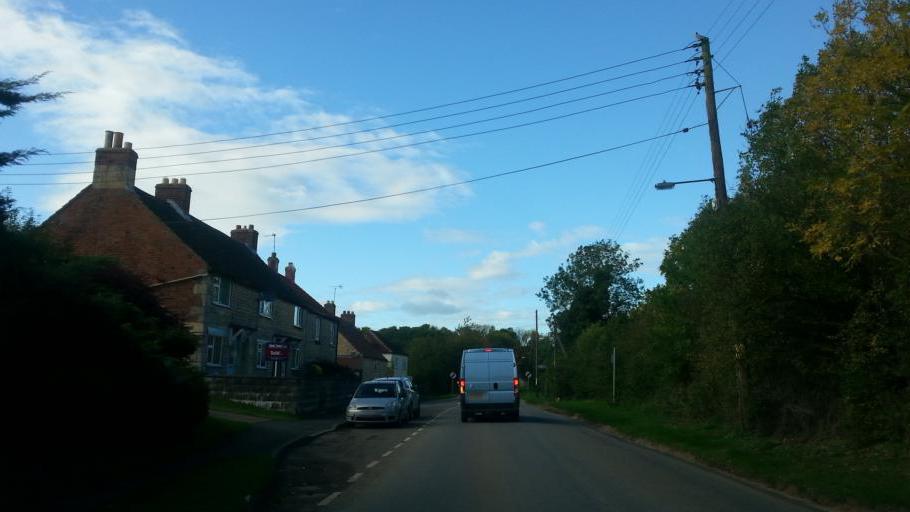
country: GB
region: England
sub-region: District of Rutland
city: Greetham
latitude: 52.8107
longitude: -0.6214
